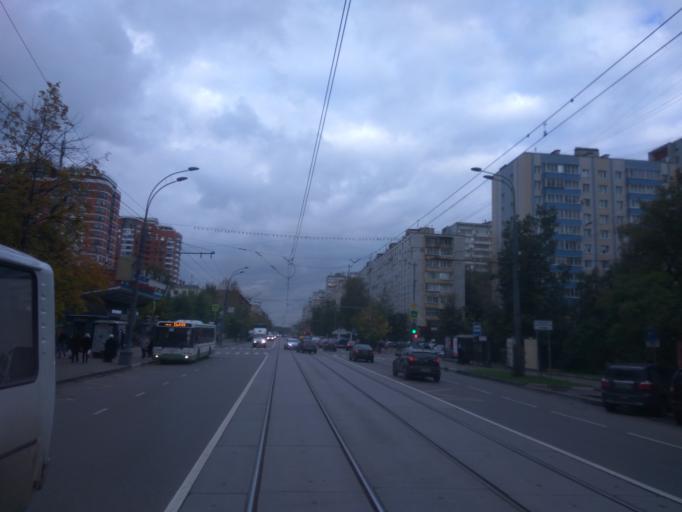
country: RU
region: Moskovskaya
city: Izmaylovo
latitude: 55.7934
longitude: 37.8045
